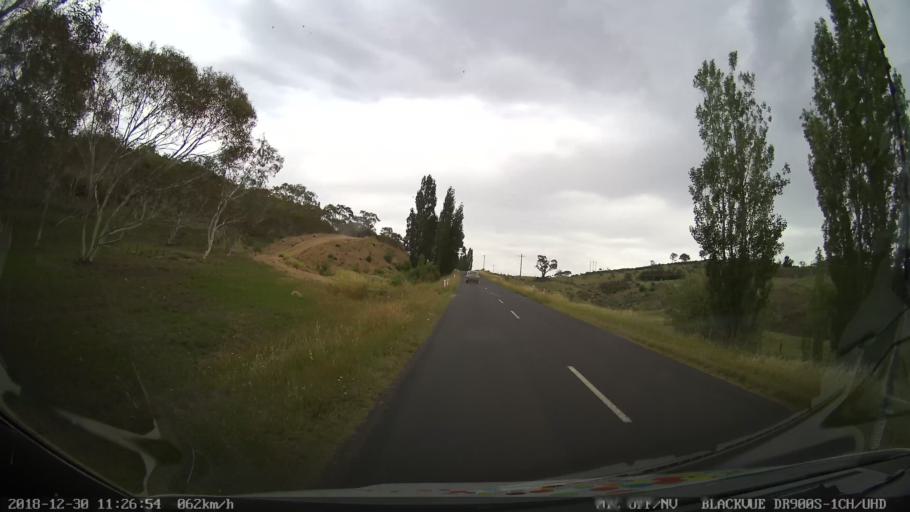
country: AU
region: New South Wales
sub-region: Snowy River
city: Jindabyne
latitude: -36.4647
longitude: 148.6303
